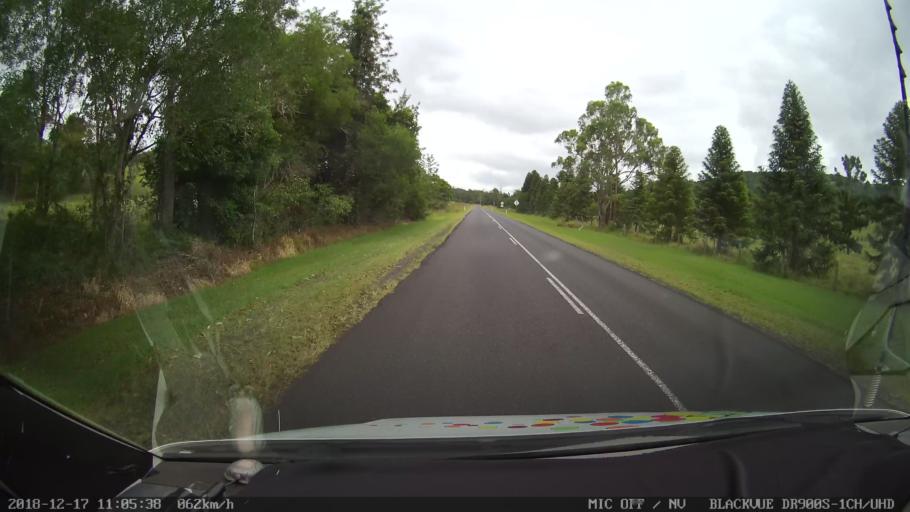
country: AU
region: New South Wales
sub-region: Kyogle
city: Kyogle
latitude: -28.7885
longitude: 152.6478
